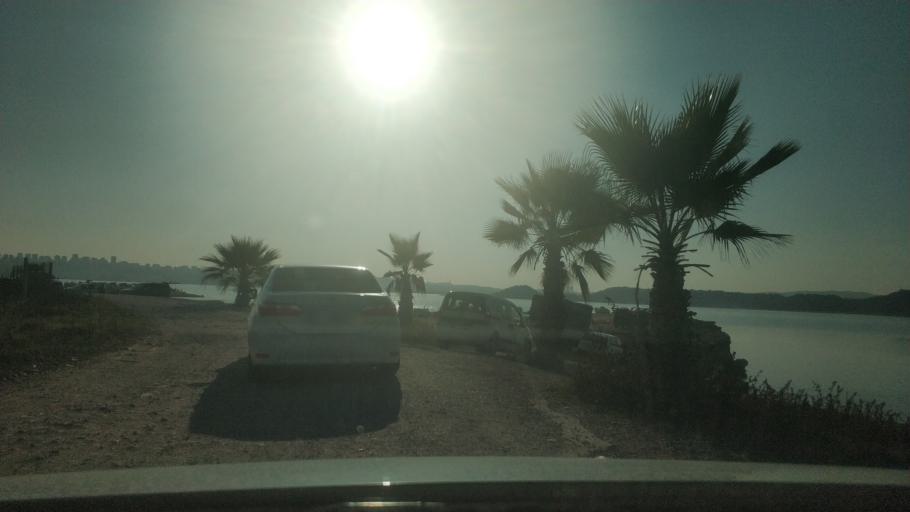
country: TR
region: Adana
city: Adana
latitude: 37.0952
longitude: 35.3001
